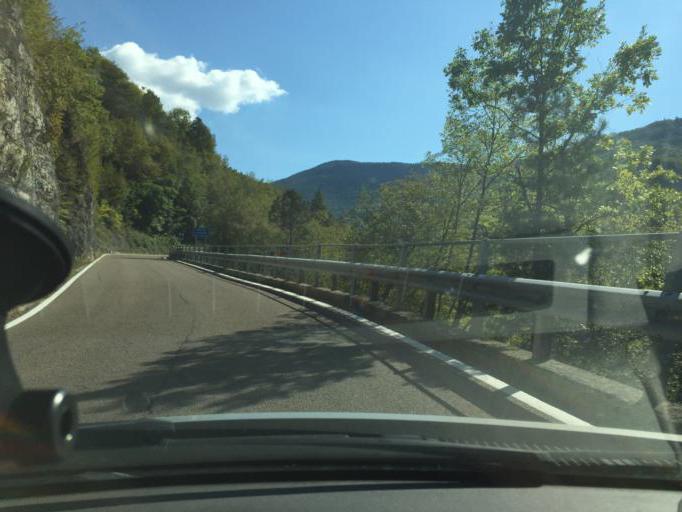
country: IT
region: Trentino-Alto Adige
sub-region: Provincia di Trento
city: Besenello
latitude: 45.9240
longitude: 11.1229
